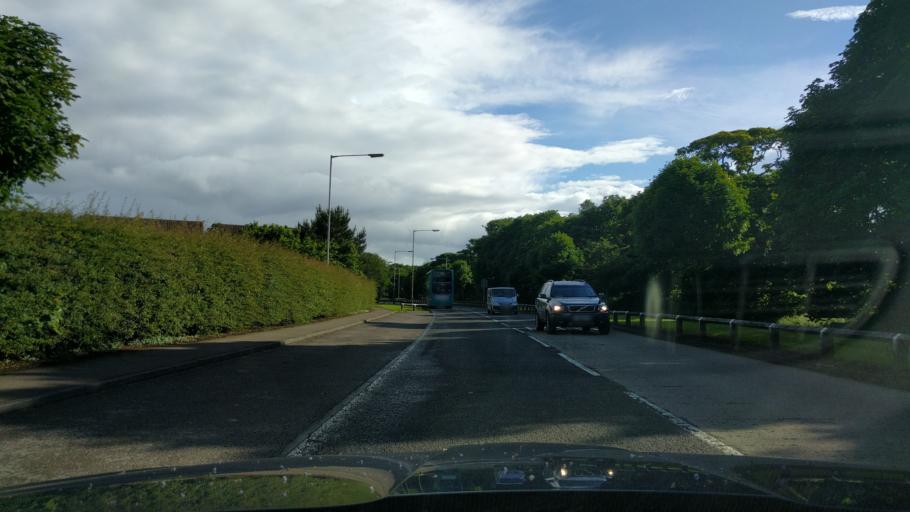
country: GB
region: England
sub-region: Northumberland
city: Cramlington
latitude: 55.0981
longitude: -1.5894
